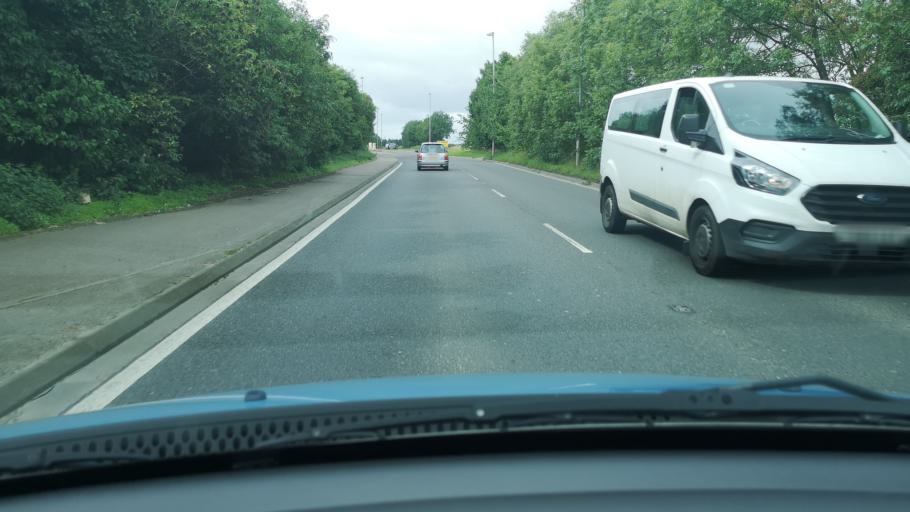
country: GB
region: England
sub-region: City and Borough of Wakefield
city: South Elmsall
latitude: 53.6044
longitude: -1.2688
